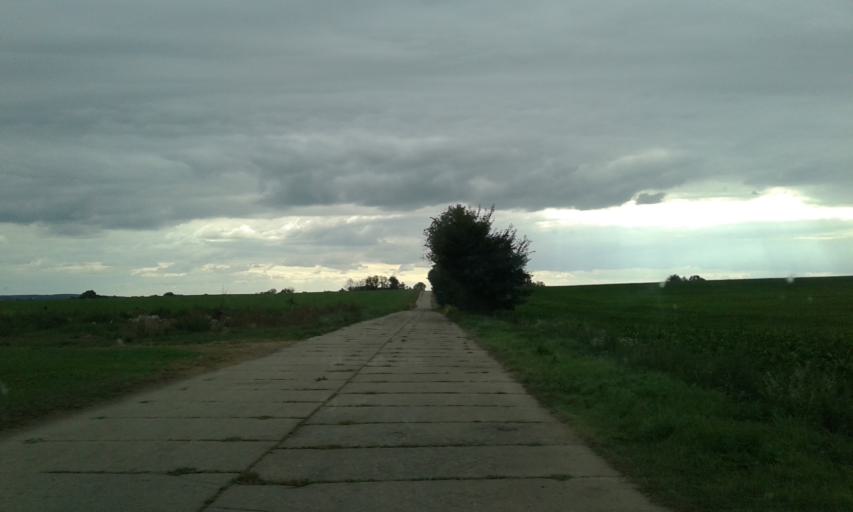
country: PL
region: West Pomeranian Voivodeship
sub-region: Powiat pyrzycki
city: Warnice
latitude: 53.1854
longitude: 15.0093
